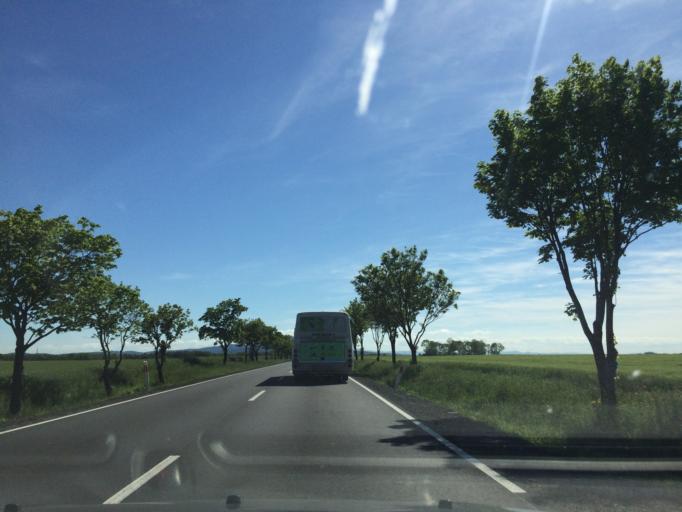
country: PL
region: Lower Silesian Voivodeship
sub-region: Powiat wroclawski
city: Gniechowice
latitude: 50.9777
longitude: 16.8140
